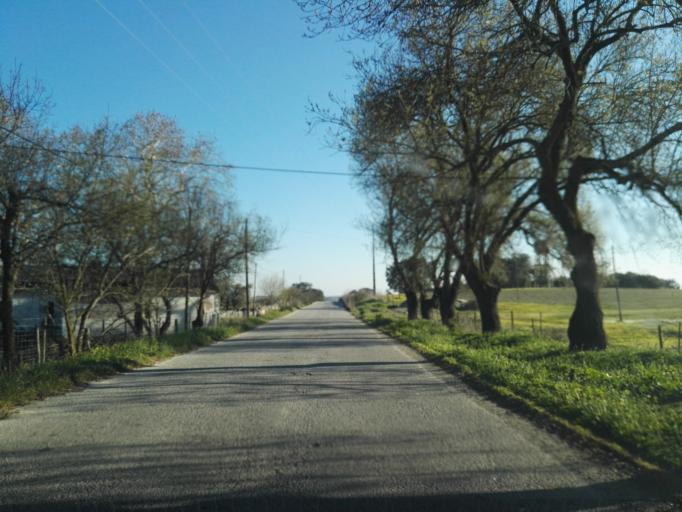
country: PT
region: Evora
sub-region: Evora
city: Evora
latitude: 38.5308
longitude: -7.9497
